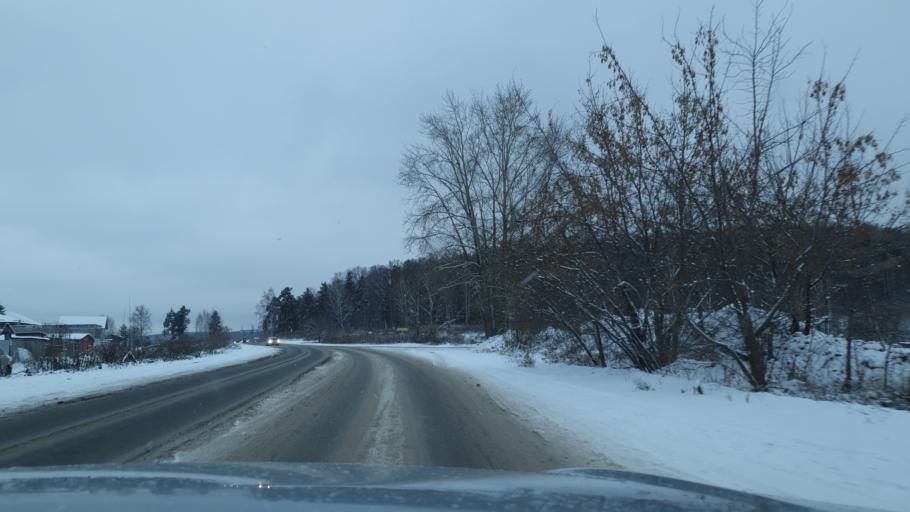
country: RU
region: Sverdlovsk
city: Istok
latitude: 56.7791
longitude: 60.7405
